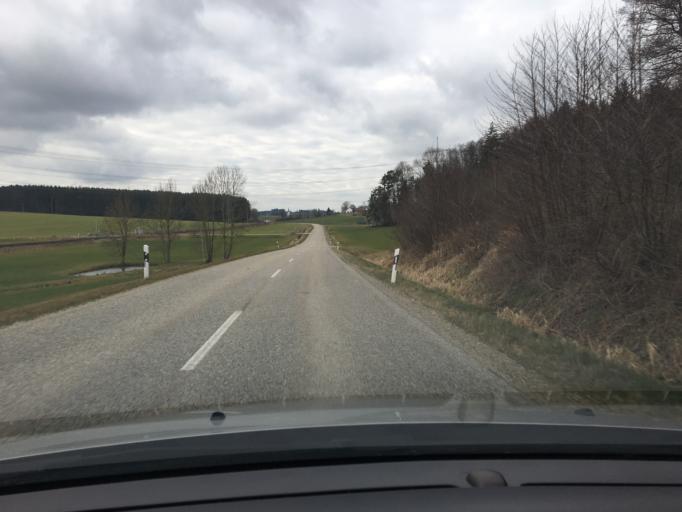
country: DE
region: Bavaria
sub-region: Lower Bavaria
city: Geisenhausen
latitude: 48.4801
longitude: 12.2377
